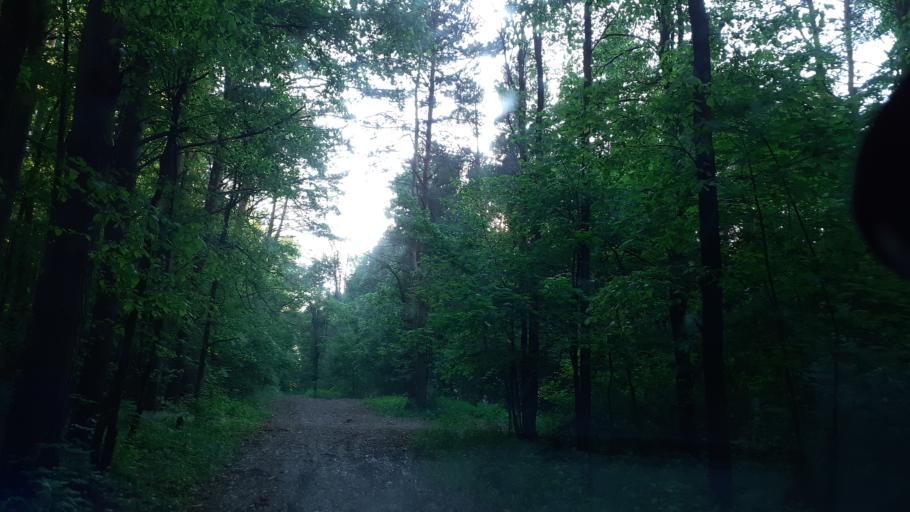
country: RU
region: Moskovskaya
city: Dubrovitsy
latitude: 55.4602
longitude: 37.5269
